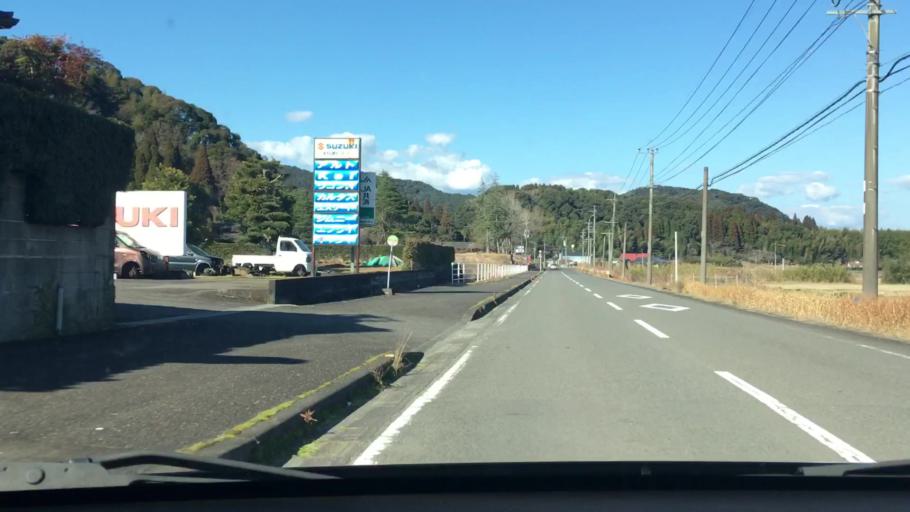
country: JP
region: Kagoshima
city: Satsumasendai
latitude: 31.7751
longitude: 130.4011
